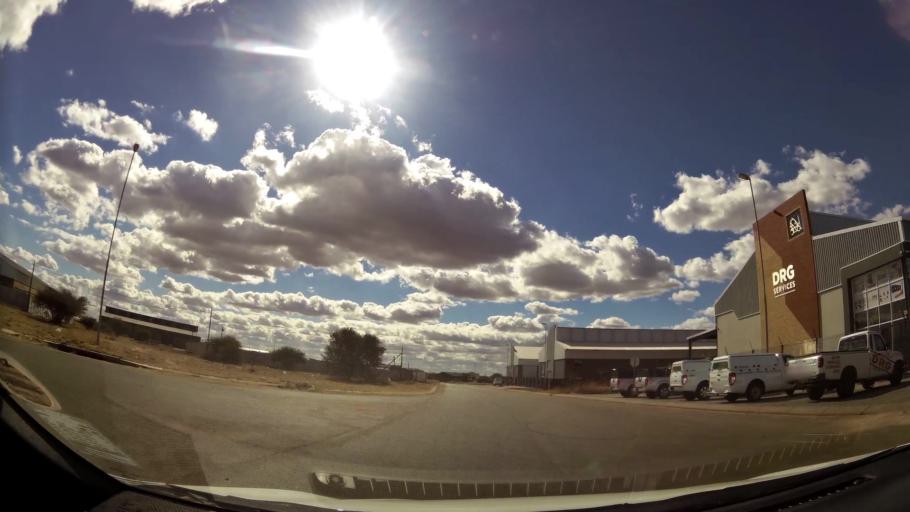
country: ZA
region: Limpopo
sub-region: Capricorn District Municipality
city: Polokwane
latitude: -23.8665
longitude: 29.4826
